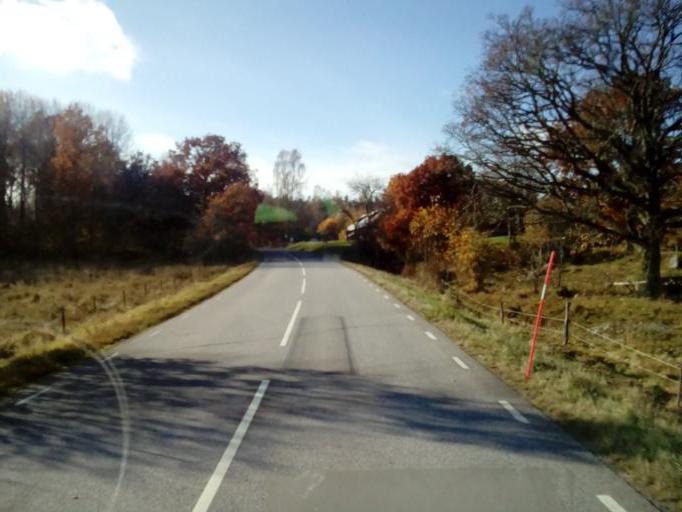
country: SE
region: Kalmar
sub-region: Vasterviks Kommun
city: Ankarsrum
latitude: 57.7589
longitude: 16.1264
